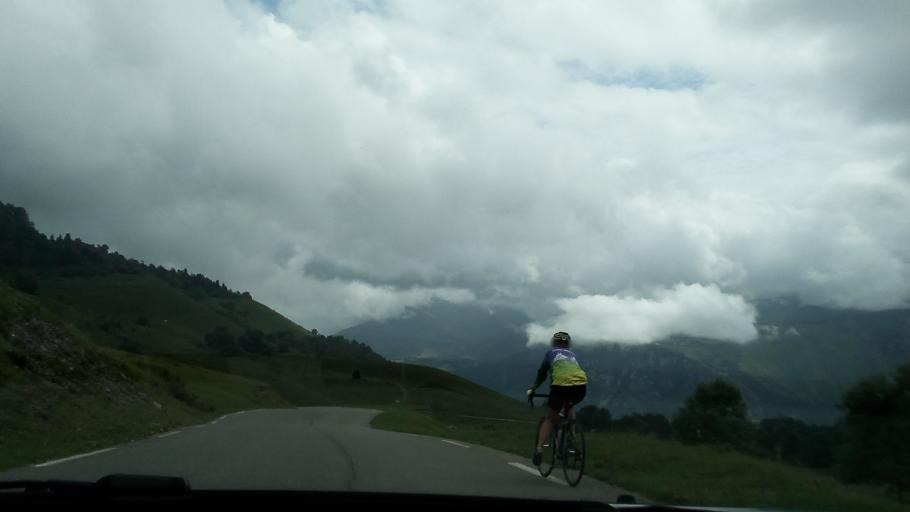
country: FR
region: Aquitaine
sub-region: Departement des Pyrenees-Atlantiques
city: Louvie-Juzon
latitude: 43.0654
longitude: -0.4649
